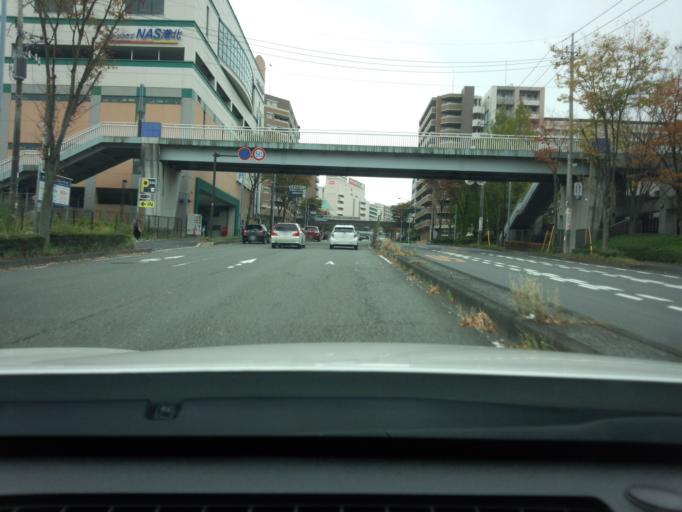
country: JP
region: Tokyo
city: Chofugaoka
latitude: 35.5481
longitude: 139.5735
